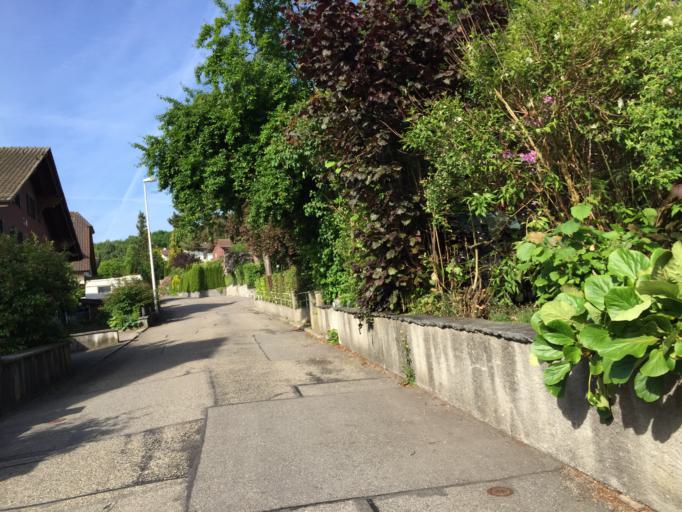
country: CH
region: Bern
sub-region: Bern-Mittelland District
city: Koniz
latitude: 46.9278
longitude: 7.4100
